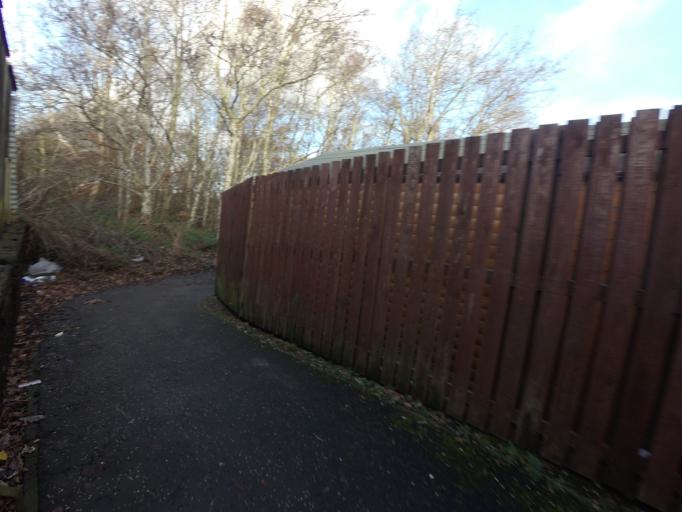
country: GB
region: Scotland
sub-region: West Lothian
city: West Calder
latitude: 55.8794
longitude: -3.5855
